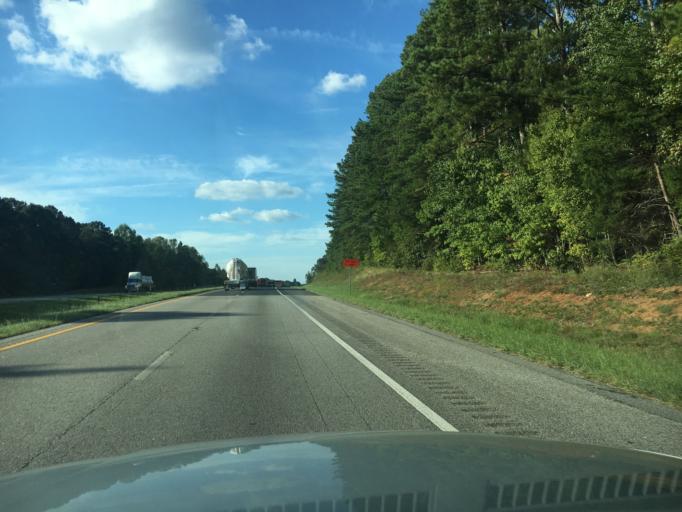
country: US
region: South Carolina
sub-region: Laurens County
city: Watts Mills
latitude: 34.6213
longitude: -81.9038
